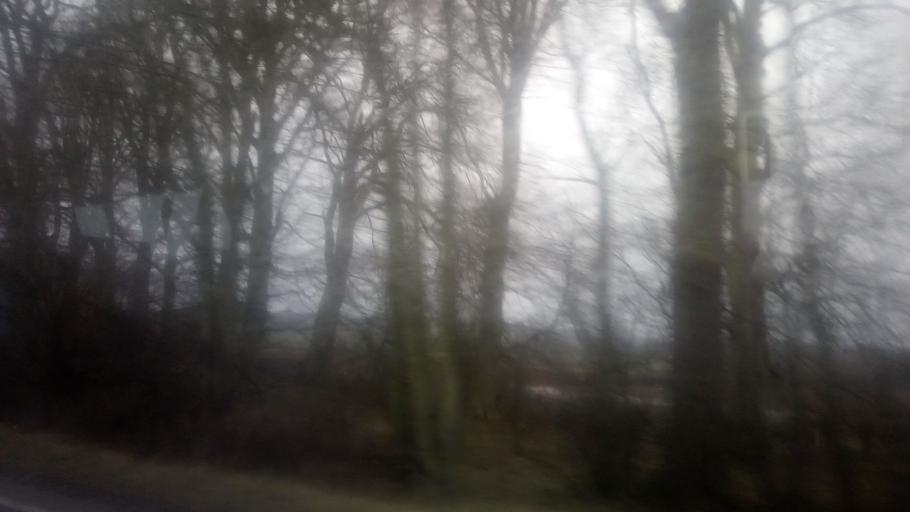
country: GB
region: Scotland
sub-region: The Scottish Borders
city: Saint Boswells
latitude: 55.5580
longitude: -2.6389
